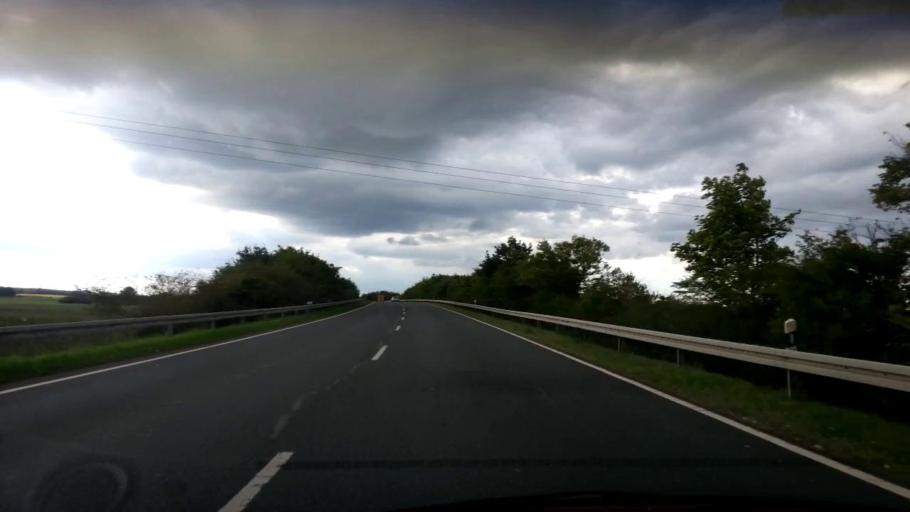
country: DE
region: Bavaria
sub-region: Regierungsbezirk Mittelfranken
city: Adelsdorf
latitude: 49.7014
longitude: 10.8872
